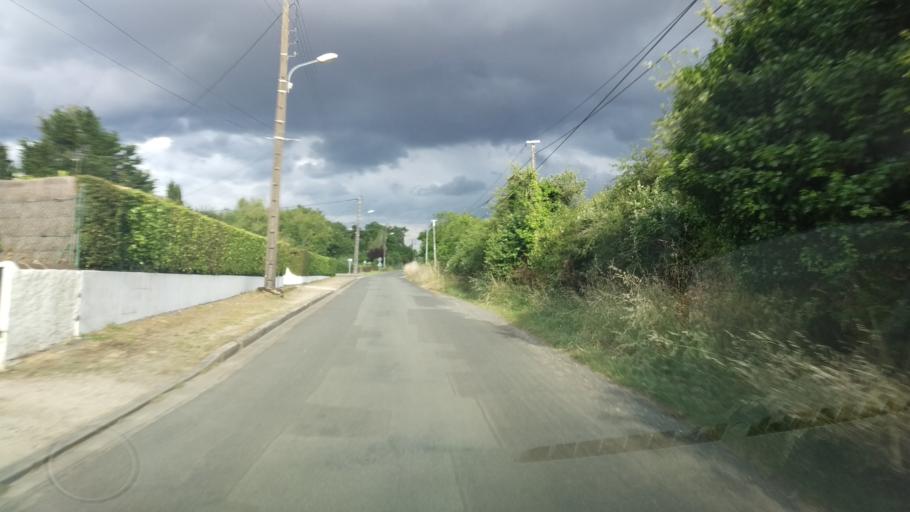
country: FR
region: Poitou-Charentes
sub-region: Departement de la Vienne
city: Migne-Auxances
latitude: 46.6256
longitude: 0.3435
